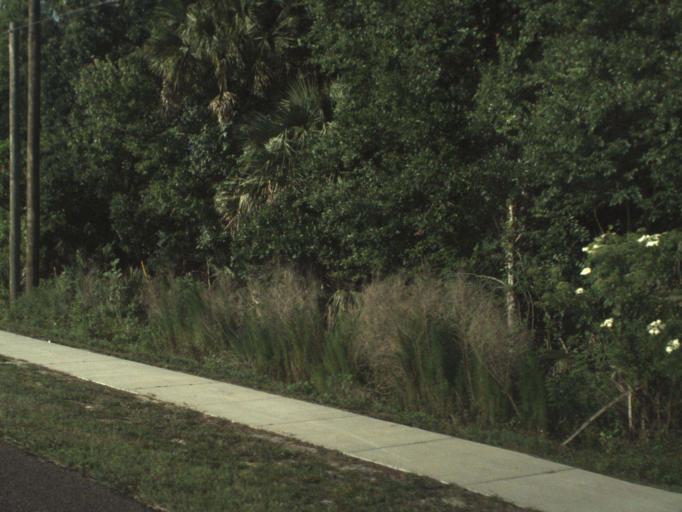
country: US
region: Florida
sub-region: Volusia County
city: Oak Hill
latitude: 28.8506
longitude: -80.8484
